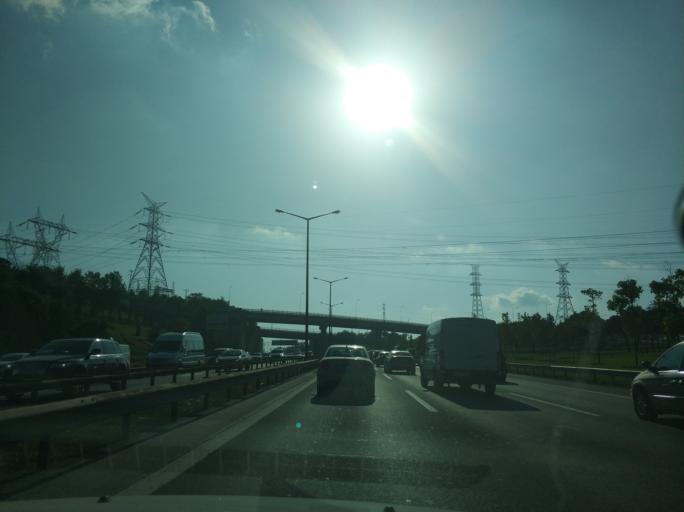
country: TR
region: Istanbul
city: Sisli
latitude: 41.0997
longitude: 28.9611
